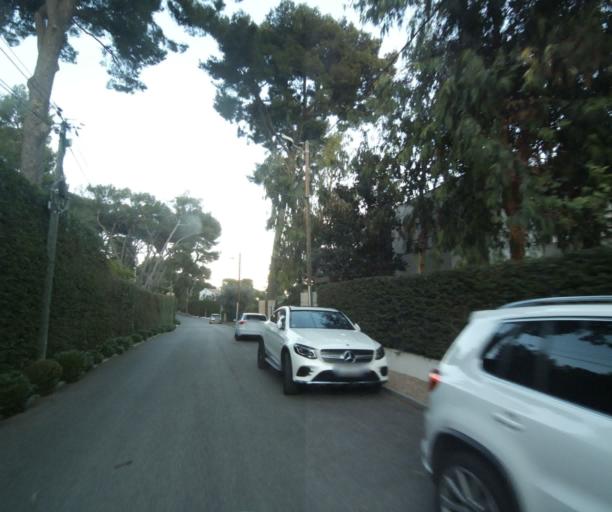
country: FR
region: Provence-Alpes-Cote d'Azur
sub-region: Departement des Alpes-Maritimes
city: Antibes
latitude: 43.5635
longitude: 7.1336
